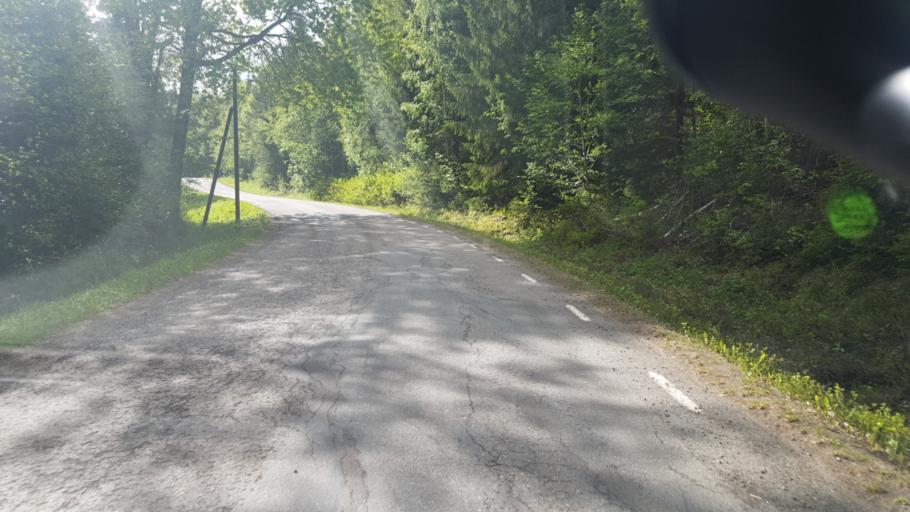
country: NO
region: Ostfold
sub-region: Romskog
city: Romskog
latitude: 59.8269
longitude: 11.9649
